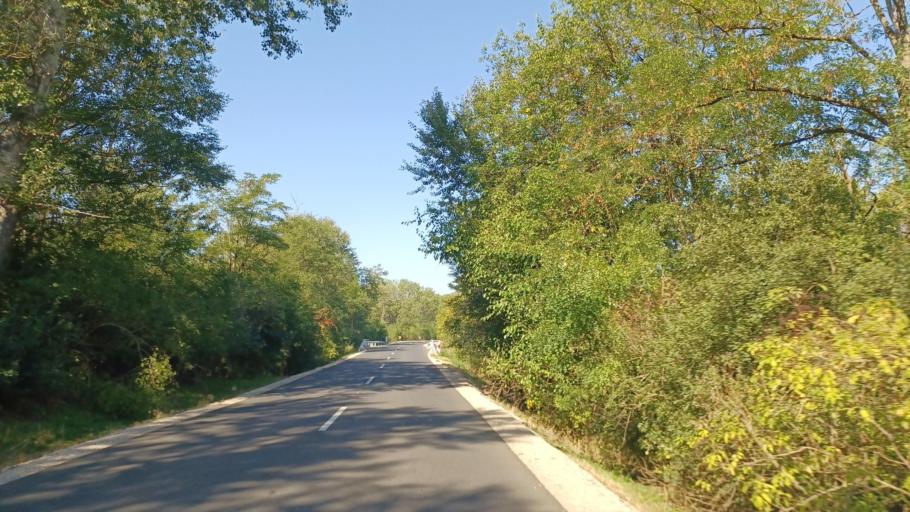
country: HU
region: Tolna
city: Nemetker
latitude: 46.7394
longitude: 18.7058
